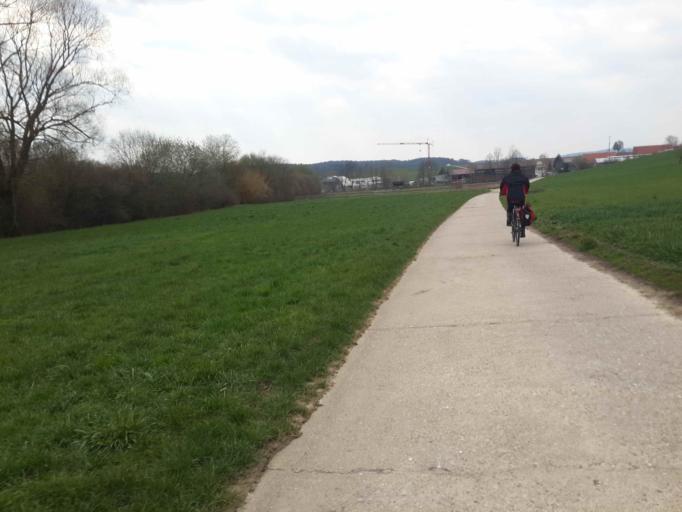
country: DE
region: Baden-Wuerttemberg
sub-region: Regierungsbezirk Stuttgart
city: Eppingen
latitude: 49.1629
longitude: 8.8957
